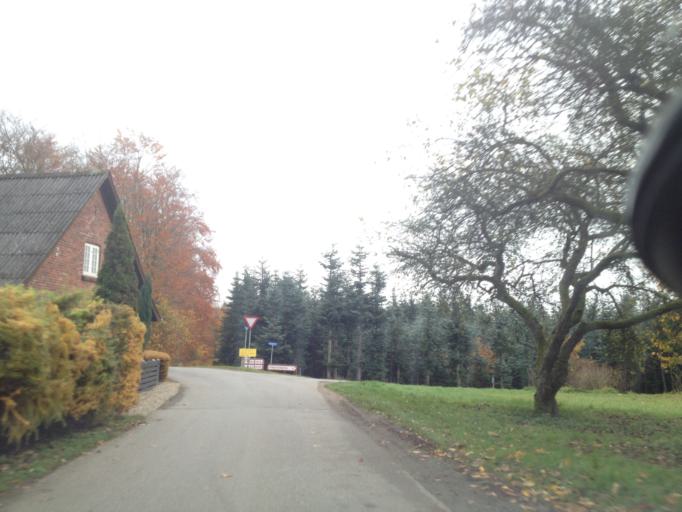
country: DK
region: South Denmark
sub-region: Assens Kommune
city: Vissenbjerg
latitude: 55.4229
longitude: 10.1957
